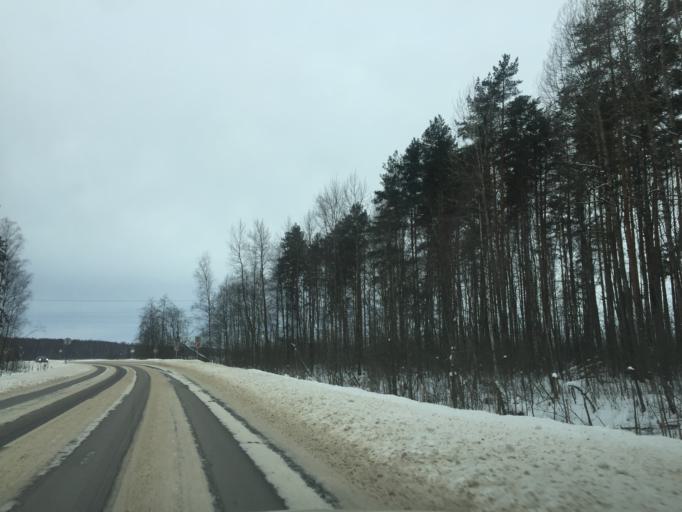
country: RU
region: Leningrad
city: Imeni Sverdlova
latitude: 59.8300
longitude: 30.6521
